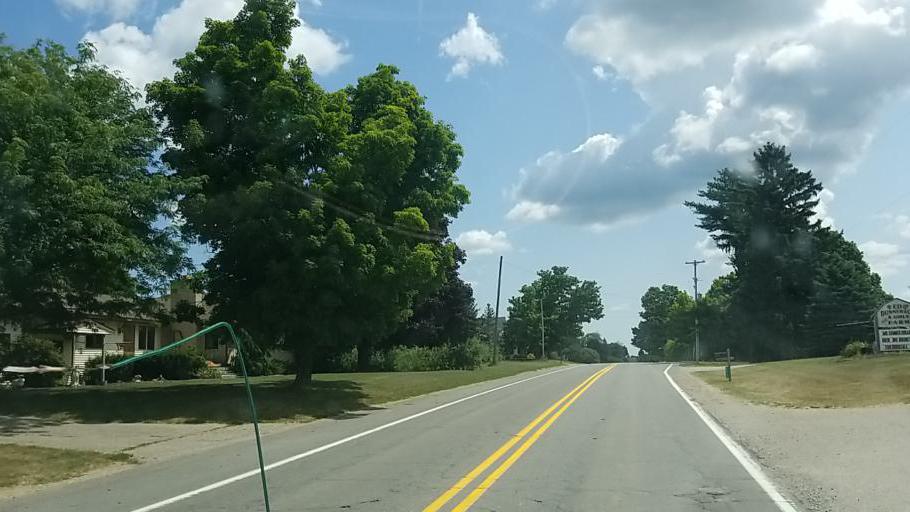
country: US
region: Michigan
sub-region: Kent County
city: Walker
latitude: 43.0591
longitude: -85.7450
